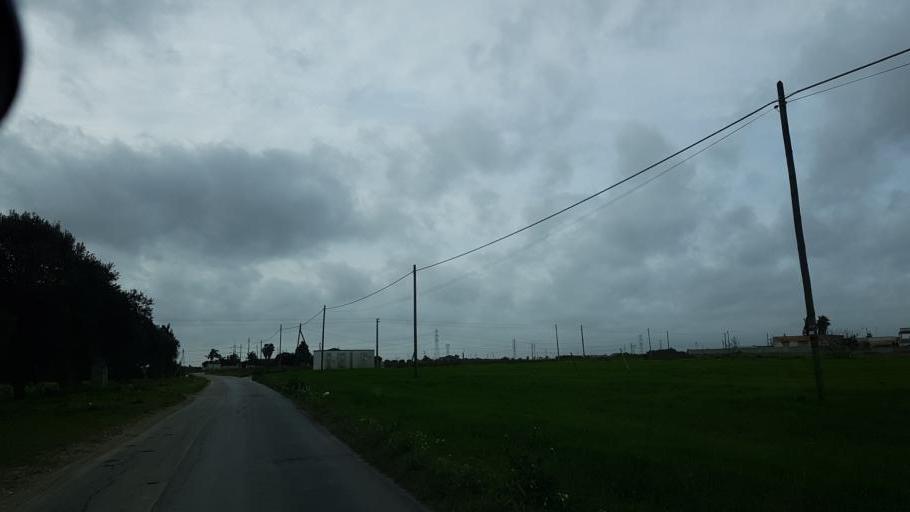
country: IT
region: Apulia
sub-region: Provincia di Brindisi
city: Brindisi
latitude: 40.6087
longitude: 17.9258
